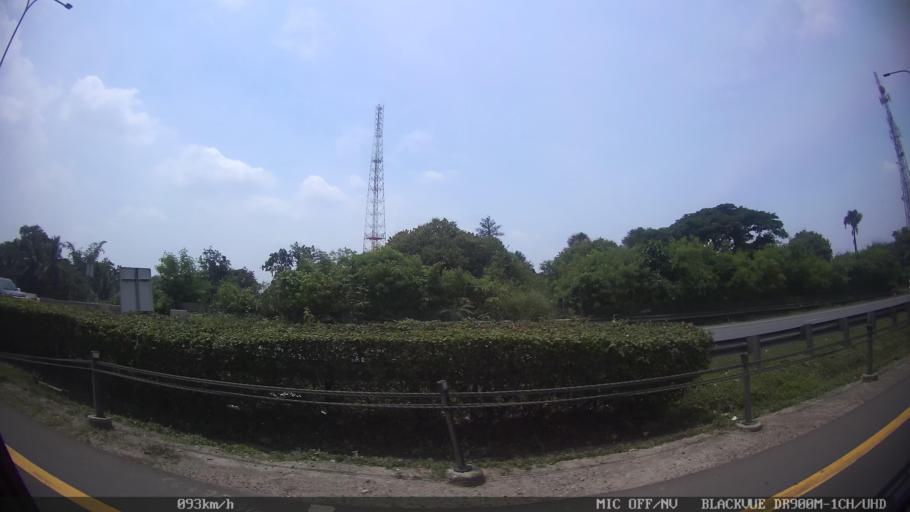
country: ID
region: West Java
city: Kresek
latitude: -6.1520
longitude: 106.3108
